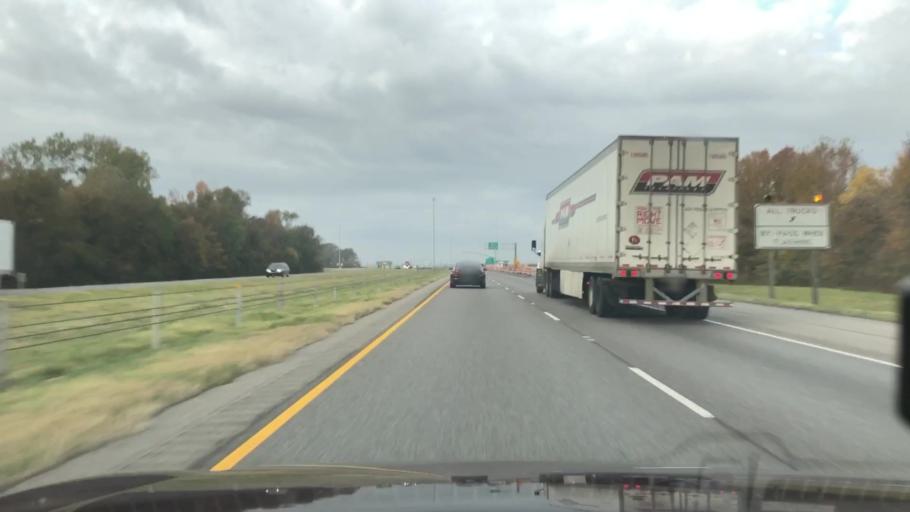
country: US
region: Mississippi
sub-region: Warren County
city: Vicksburg
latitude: 32.3209
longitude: -90.9419
